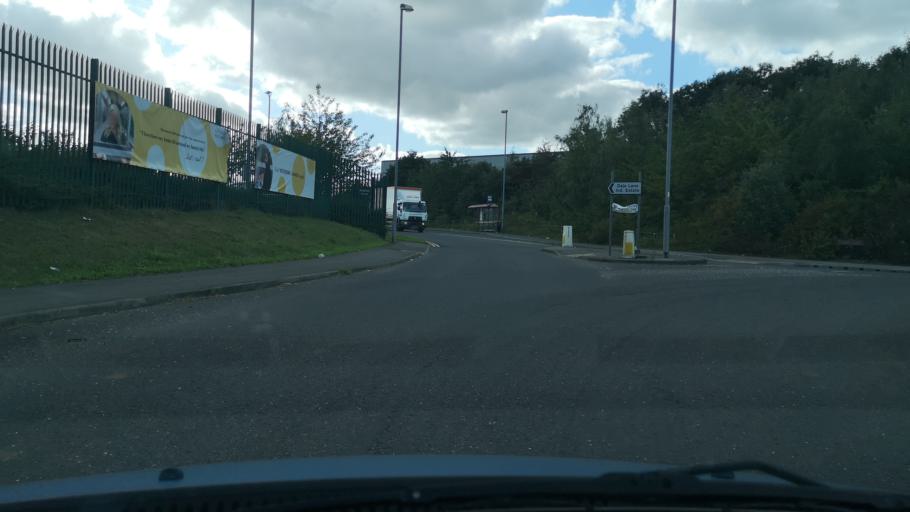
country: GB
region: England
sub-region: City and Borough of Wakefield
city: North Elmsall
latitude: 53.6048
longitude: -1.2705
